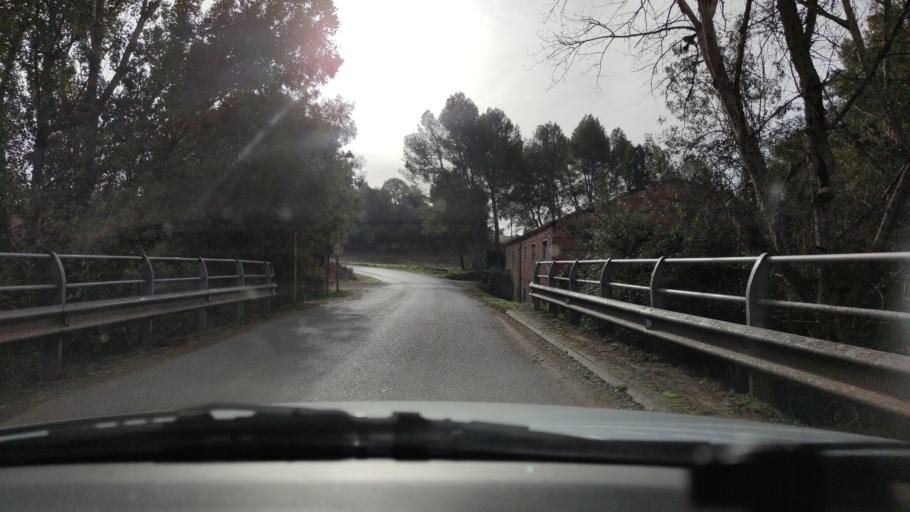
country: ES
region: Catalonia
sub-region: Provincia de Lleida
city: Artesa de Segre
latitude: 41.9190
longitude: 1.0166
